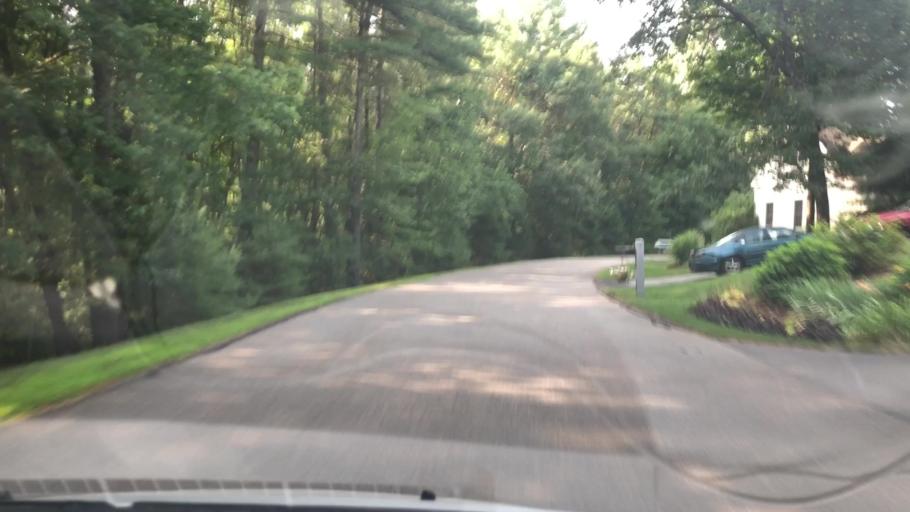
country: US
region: New Hampshire
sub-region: Hillsborough County
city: Milford
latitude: 42.8405
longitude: -71.6257
